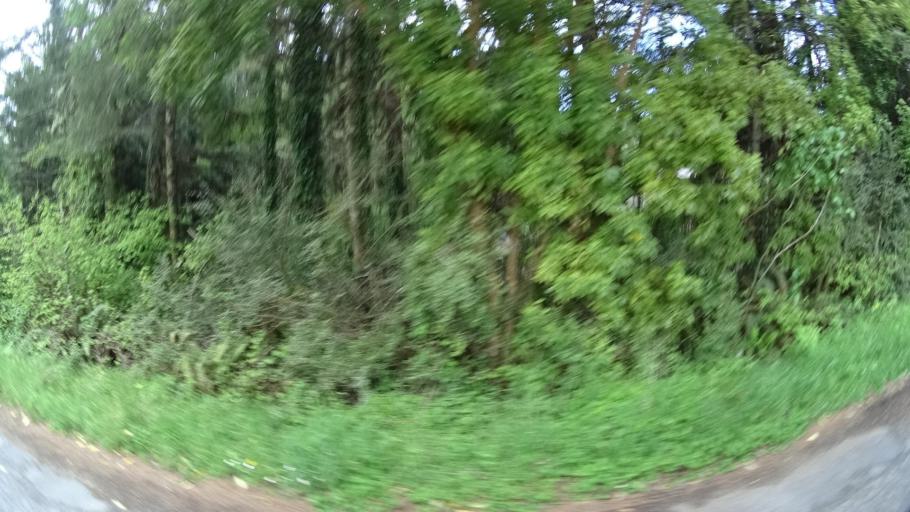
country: US
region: California
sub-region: Humboldt County
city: Bayside
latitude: 40.8480
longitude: -124.0543
